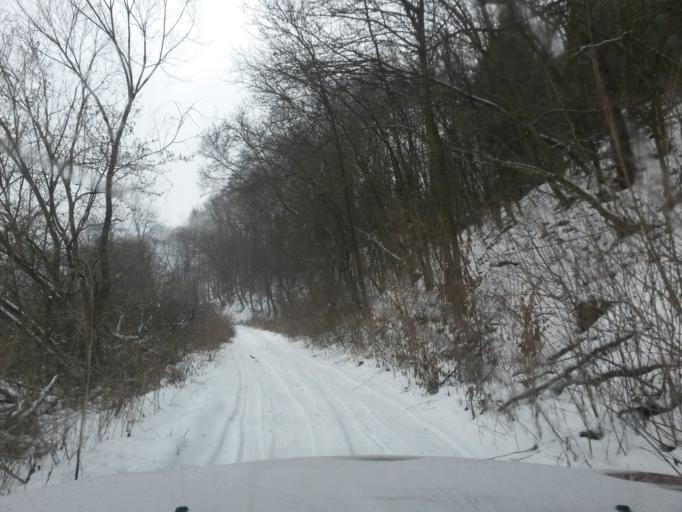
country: SK
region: Presovsky
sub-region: Okres Presov
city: Presov
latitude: 48.8985
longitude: 21.2030
